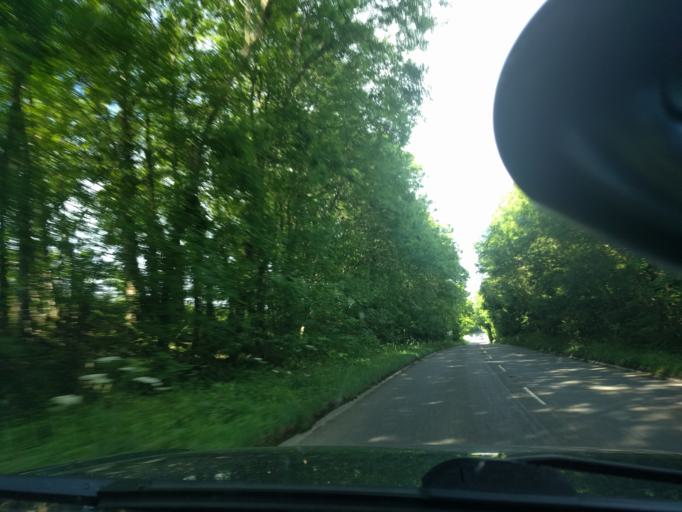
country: GB
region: England
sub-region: Wiltshire
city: Lyneham
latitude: 51.5261
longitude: -1.9428
